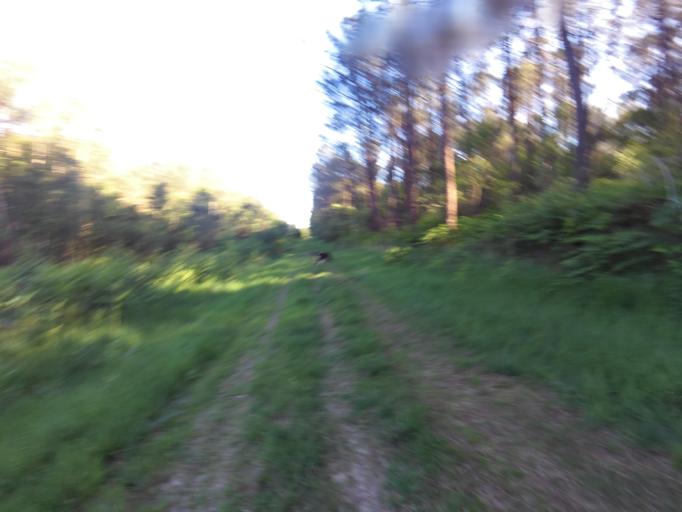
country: FR
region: Brittany
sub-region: Departement du Morbihan
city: Molac
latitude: 47.7449
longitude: -2.4301
